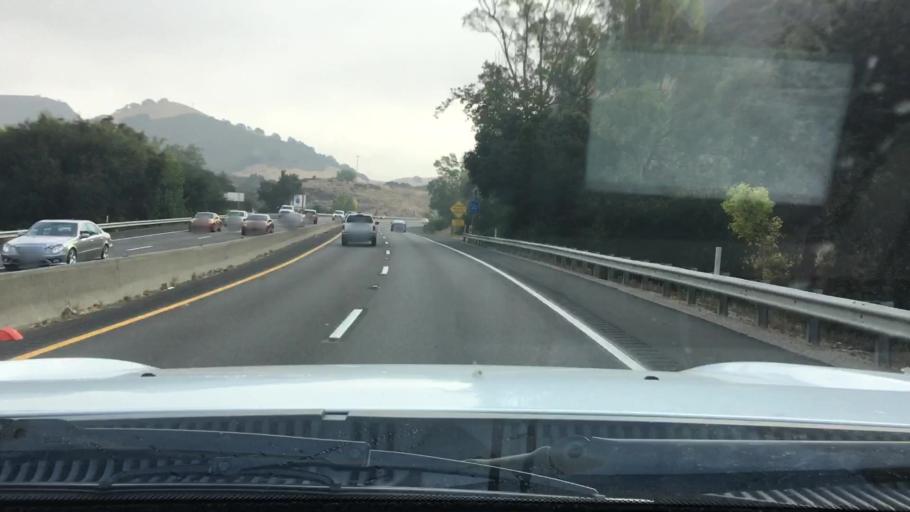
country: US
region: California
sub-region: San Luis Obispo County
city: San Luis Obispo
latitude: 35.2916
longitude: -120.6495
